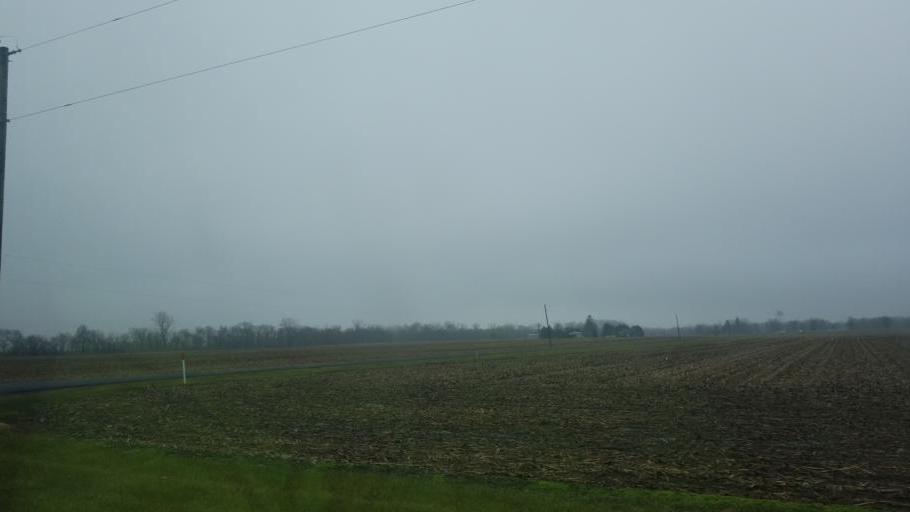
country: US
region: Ohio
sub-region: Champaign County
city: North Lewisburg
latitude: 40.2347
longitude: -83.5423
